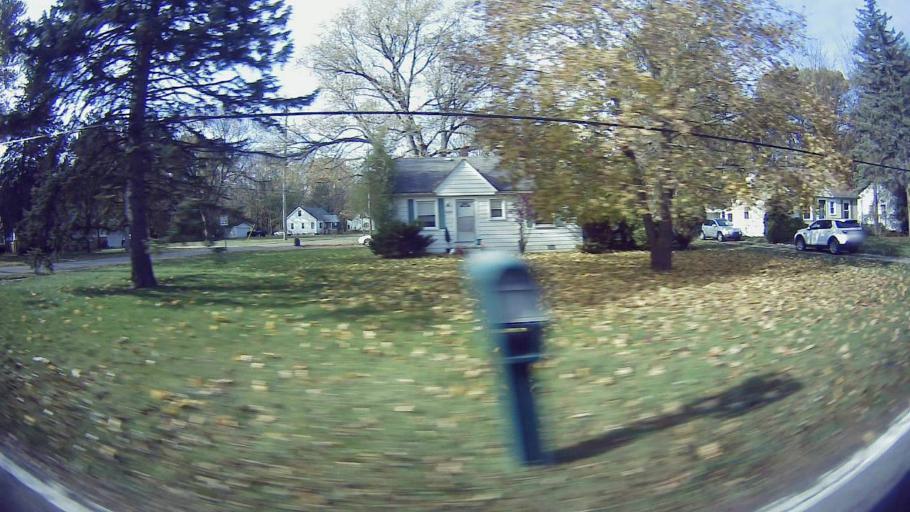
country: US
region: Michigan
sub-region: Oakland County
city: Southfield
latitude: 42.4565
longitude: -83.2729
